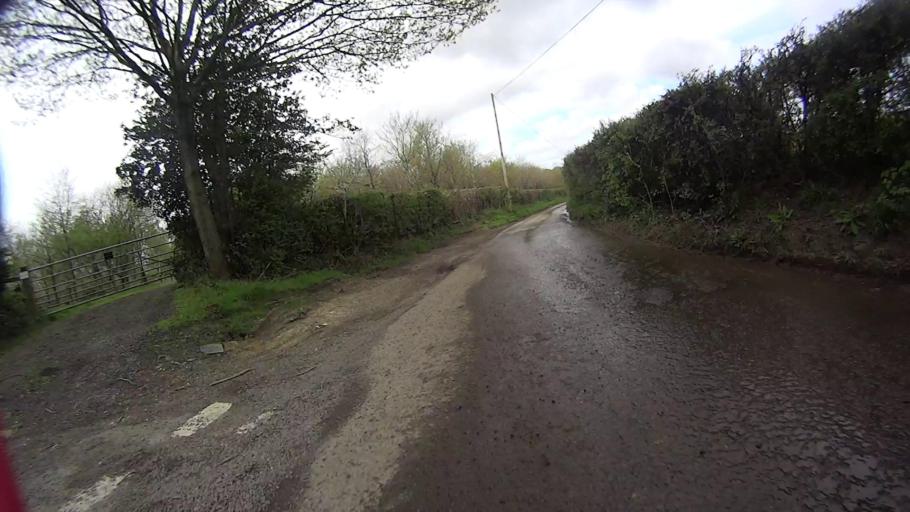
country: GB
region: England
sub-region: West Sussex
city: Horsham
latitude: 51.1080
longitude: -0.3049
